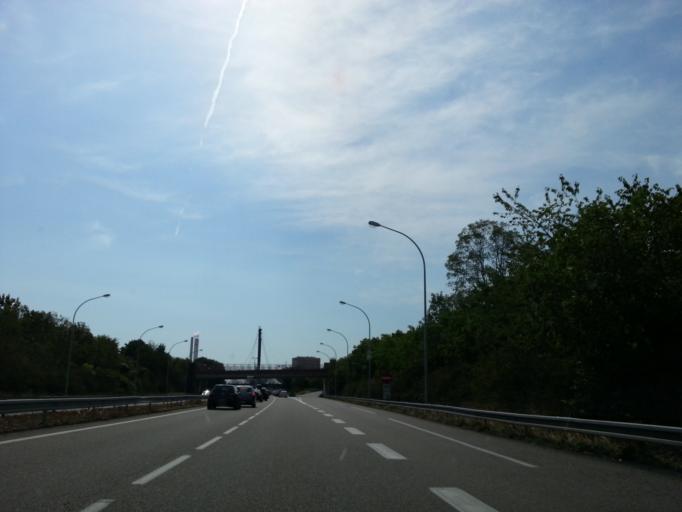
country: FR
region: Alsace
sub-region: Departement du Haut-Rhin
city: Saint-Louis
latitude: 47.5796
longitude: 7.5562
